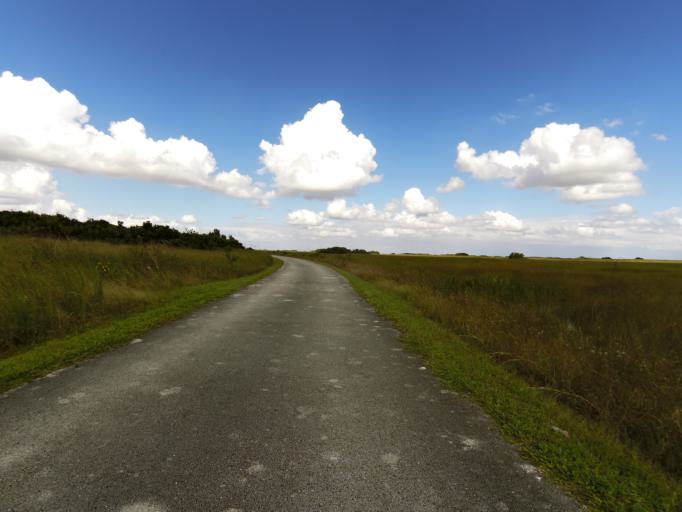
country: US
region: Florida
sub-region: Miami-Dade County
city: The Hammocks
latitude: 25.6700
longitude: -80.7599
